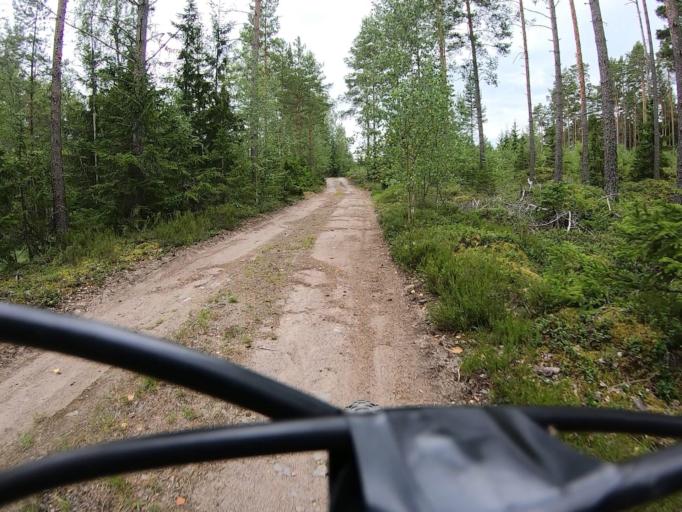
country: FI
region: Varsinais-Suomi
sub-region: Vakka-Suomi
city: Uusikaupunki
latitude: 60.8516
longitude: 21.4213
